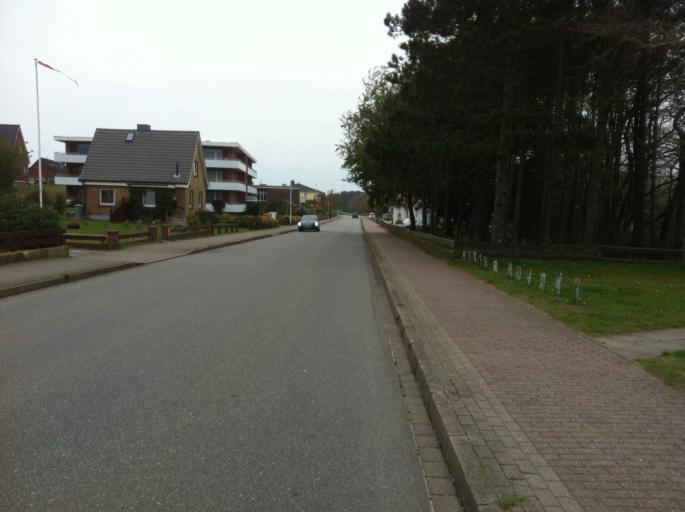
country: DE
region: Schleswig-Holstein
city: Wittdun
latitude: 54.6271
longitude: 8.3884
